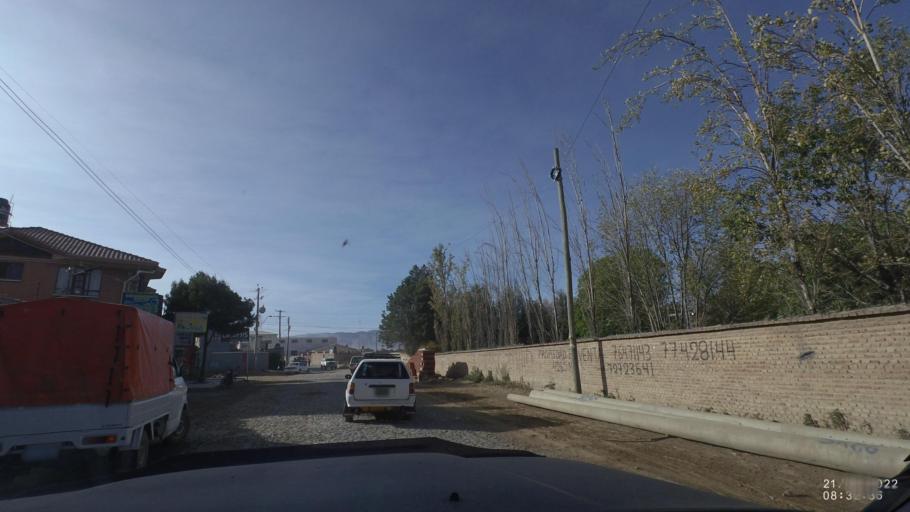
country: BO
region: Cochabamba
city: Cochabamba
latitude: -17.3855
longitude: -66.0532
